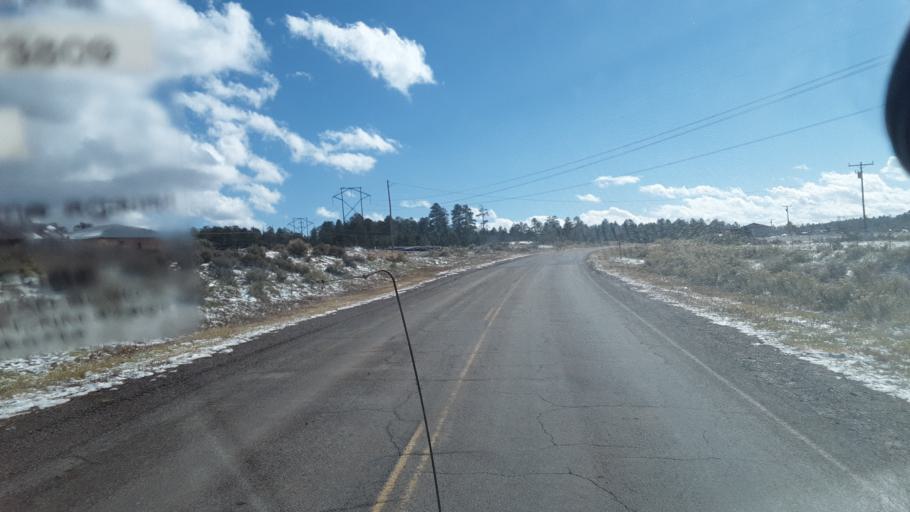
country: US
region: New Mexico
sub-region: Rio Arriba County
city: Santa Teresa
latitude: 36.2156
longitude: -106.7810
